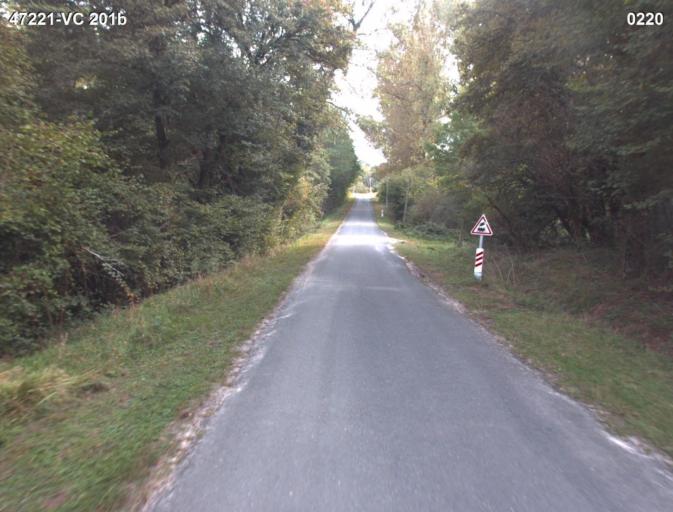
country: FR
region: Aquitaine
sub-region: Departement du Lot-et-Garonne
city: Mezin
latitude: 44.0767
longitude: 0.2444
